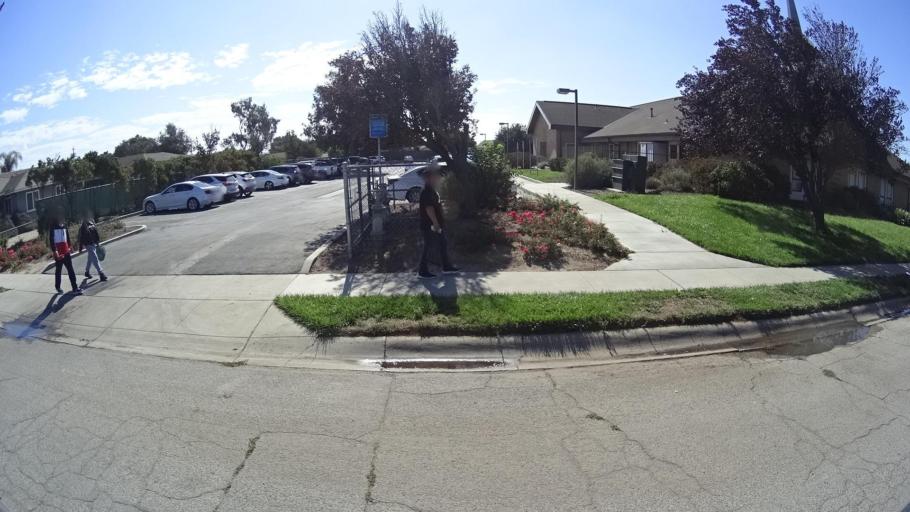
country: US
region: California
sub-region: Monterey County
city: Greenfield
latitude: 36.3185
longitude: -121.2474
